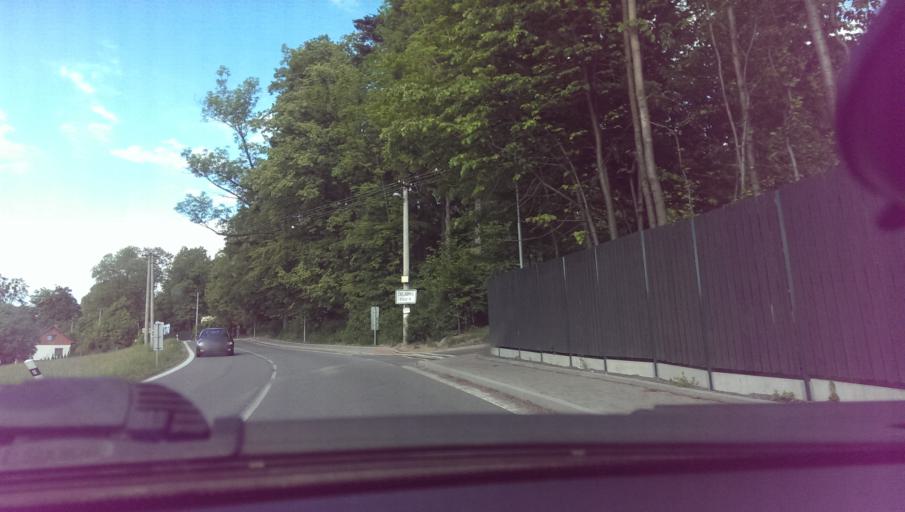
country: CZ
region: Moravskoslezsky
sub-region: Okres Frydek-Mistek
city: Celadna
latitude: 49.5388
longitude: 18.3089
